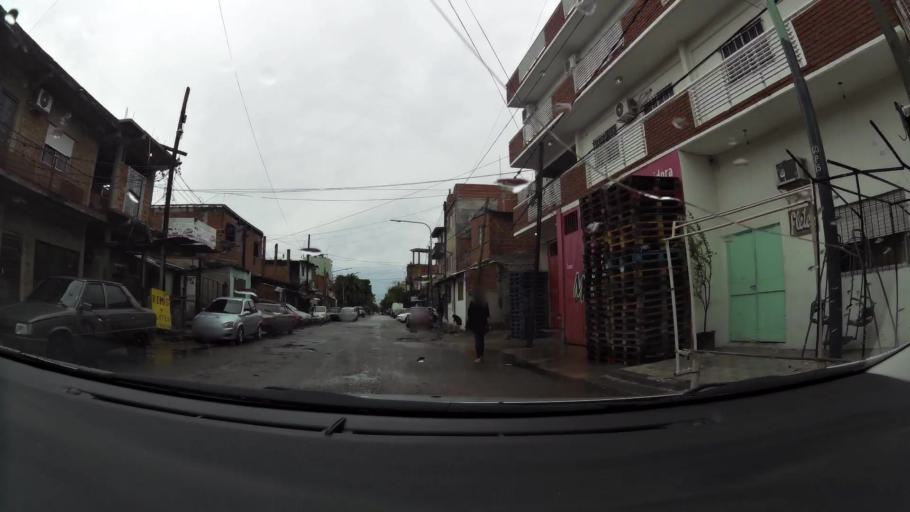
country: AR
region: Buenos Aires F.D.
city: Villa Lugano
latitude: -34.6590
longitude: -58.4543
